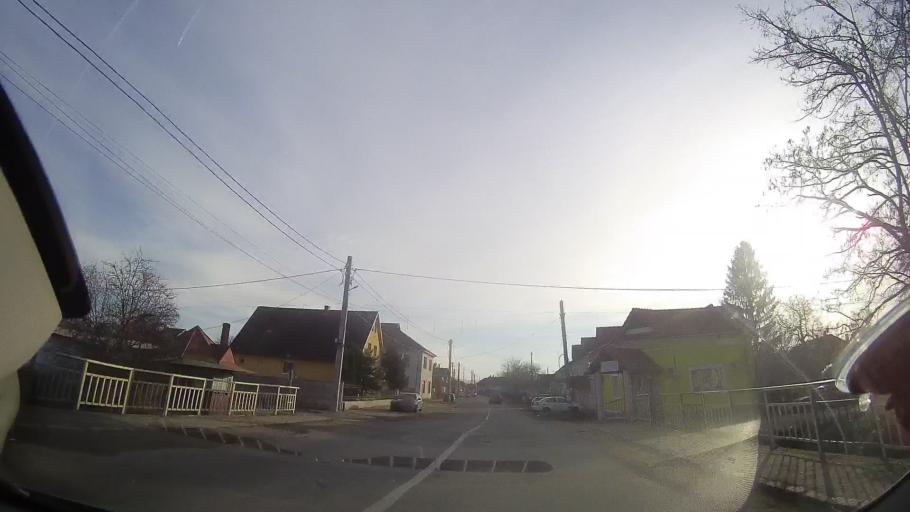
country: RO
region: Bihor
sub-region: Comuna Tileagd
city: Tileagd
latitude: 47.0709
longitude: 22.1999
